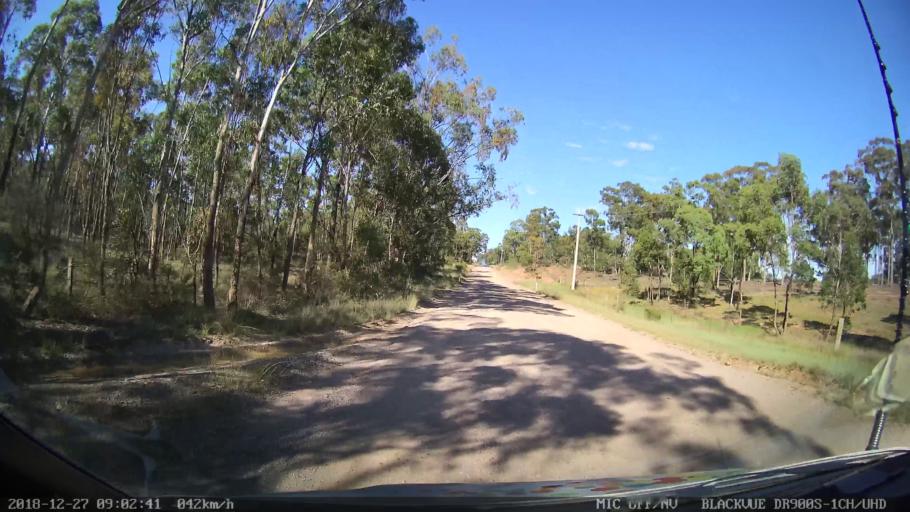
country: AU
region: New South Wales
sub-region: Lithgow
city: Portland
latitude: -33.1031
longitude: 150.2077
